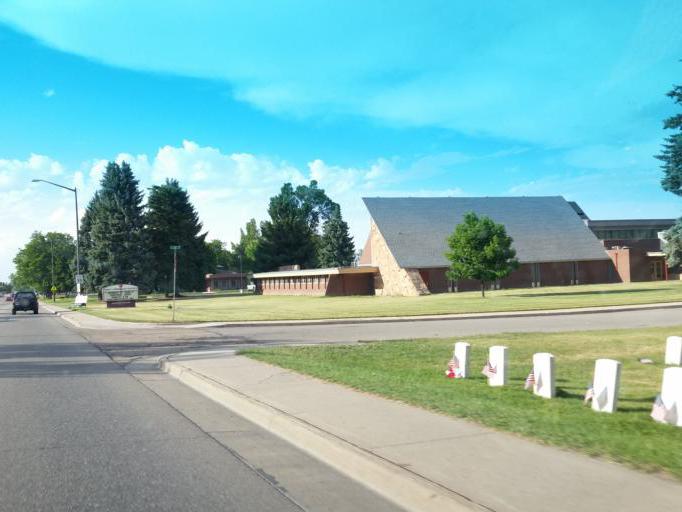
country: US
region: Colorado
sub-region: Larimer County
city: Loveland
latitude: 40.4125
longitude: -105.0730
